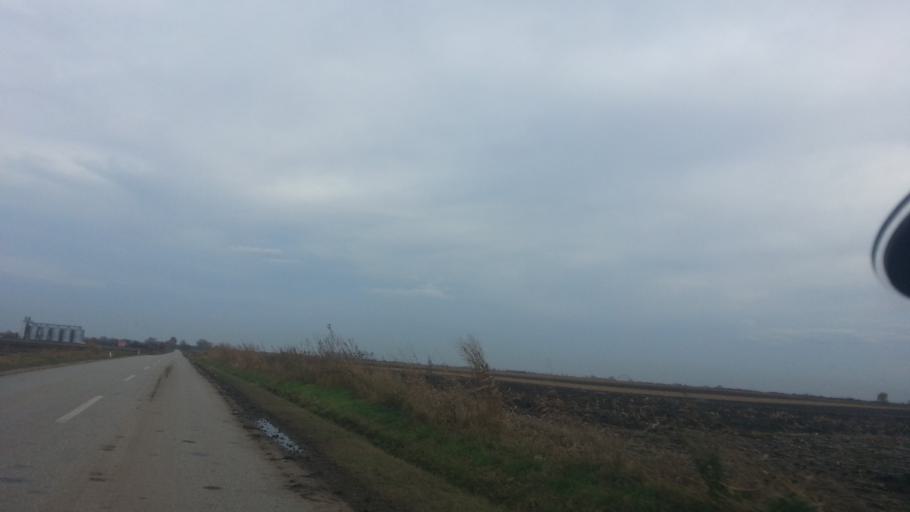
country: RS
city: Ljukovo
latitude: 44.9884
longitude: 20.0218
